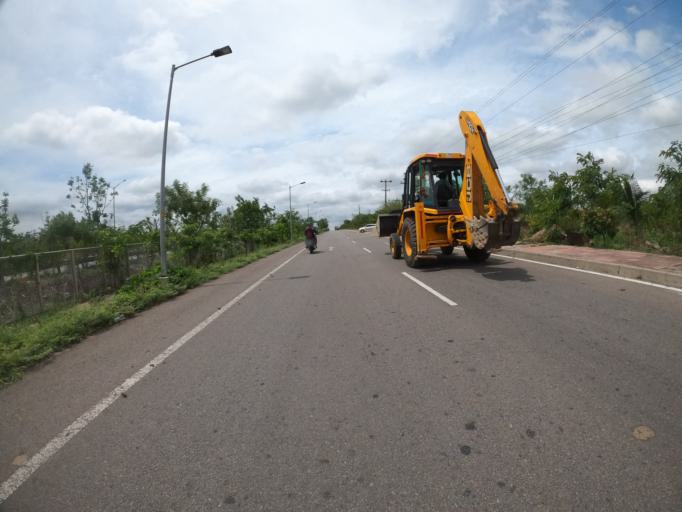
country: IN
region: Telangana
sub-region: Hyderabad
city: Hyderabad
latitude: 17.2913
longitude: 78.3810
